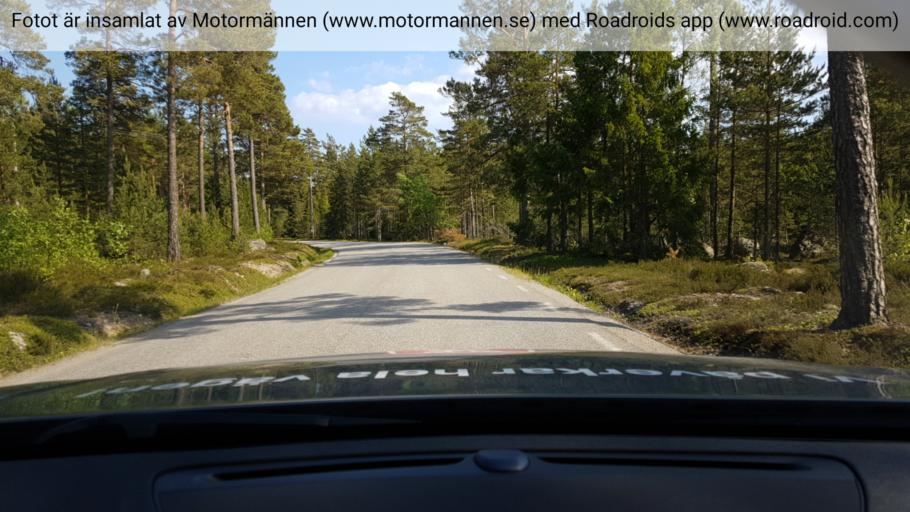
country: SE
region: Stockholm
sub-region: Varmdo Kommun
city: Mortnas
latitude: 59.2564
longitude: 18.4426
